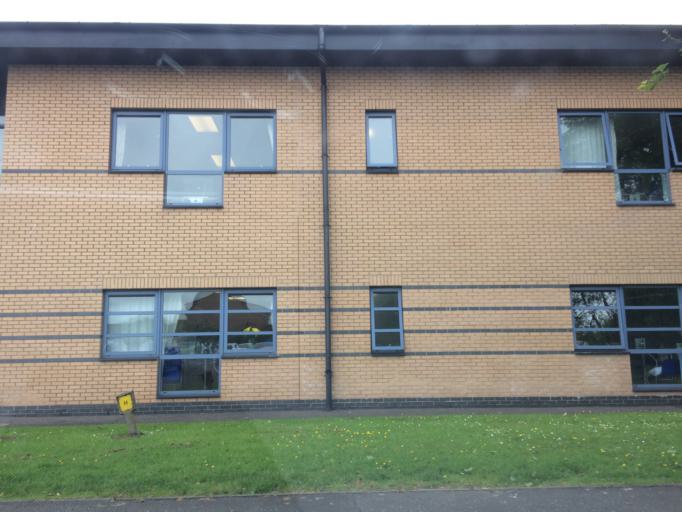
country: GB
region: Scotland
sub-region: Renfrewshire
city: Renfrew
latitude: 55.8596
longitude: -4.3432
